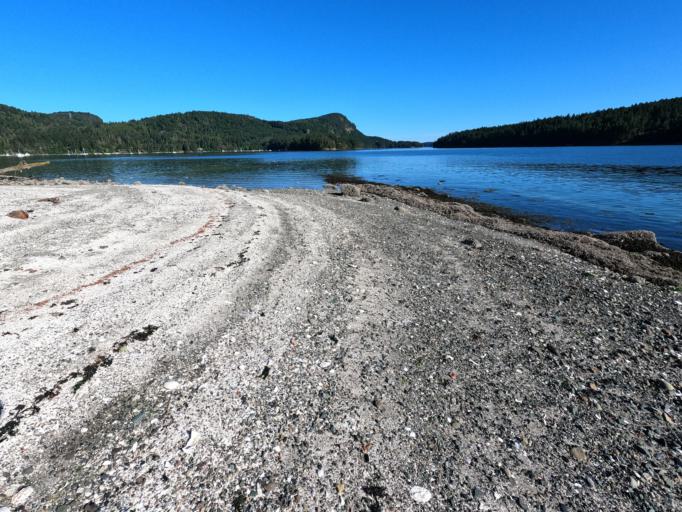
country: CA
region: British Columbia
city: North Saanich
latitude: 48.8935
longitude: -123.4067
